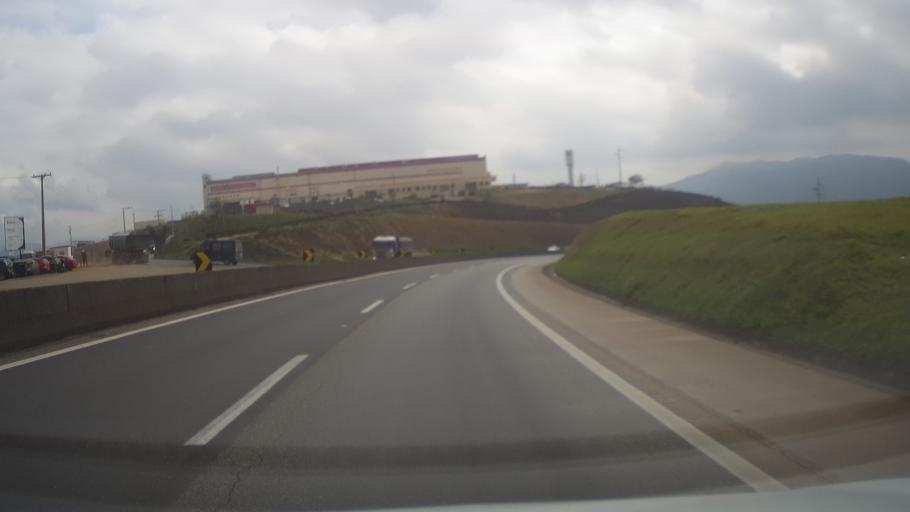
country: BR
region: Minas Gerais
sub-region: Extrema
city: Extrema
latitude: -22.8359
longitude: -46.3261
